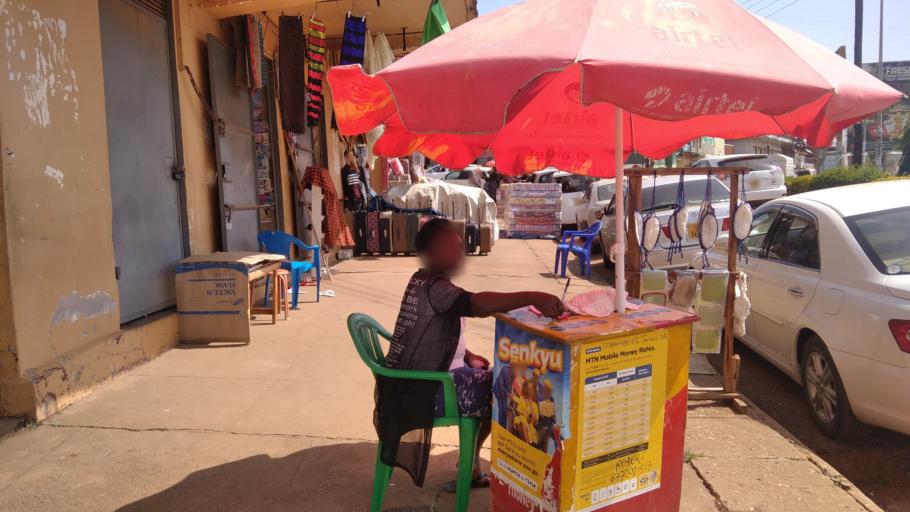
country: UG
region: Central Region
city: Masaka
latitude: -0.3424
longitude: 31.7384
